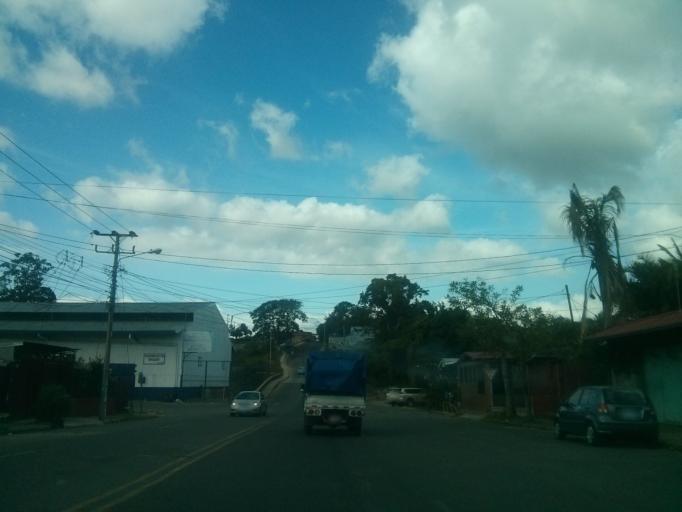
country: CR
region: San Jose
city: San Miguel
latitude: 9.8951
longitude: -84.0565
